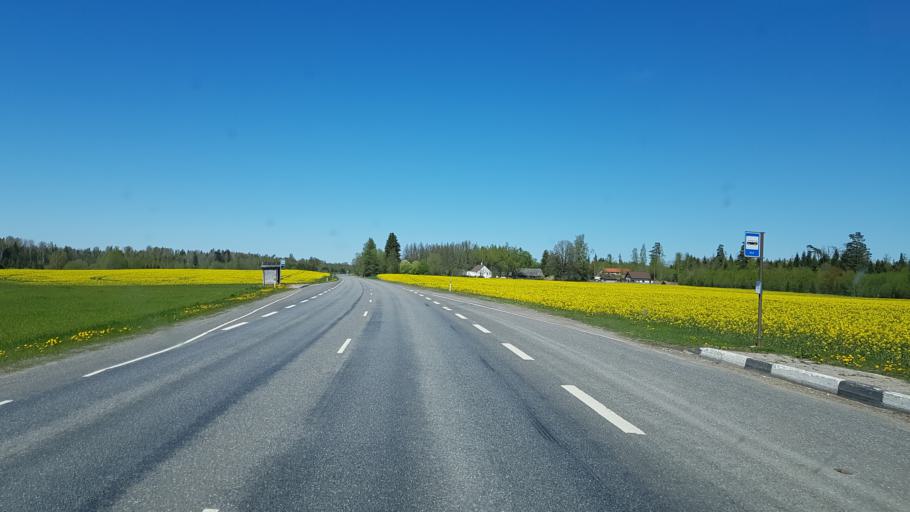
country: EE
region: Viljandimaa
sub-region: Viljandi linn
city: Viljandi
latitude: 58.4243
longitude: 25.5983
